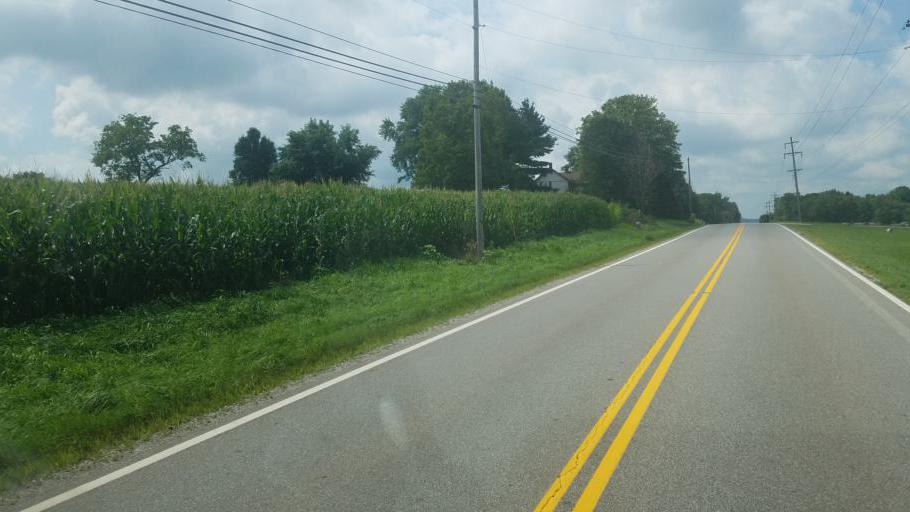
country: US
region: Ohio
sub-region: Fairfield County
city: Lancaster
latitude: 39.6526
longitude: -82.7214
